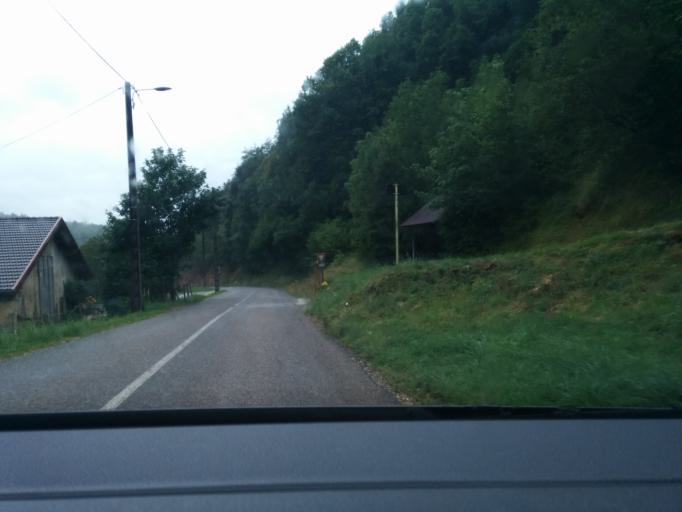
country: FR
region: Franche-Comte
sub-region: Departement du Jura
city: Valfin-les-Saint-Claude
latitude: 46.4501
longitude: 5.8259
